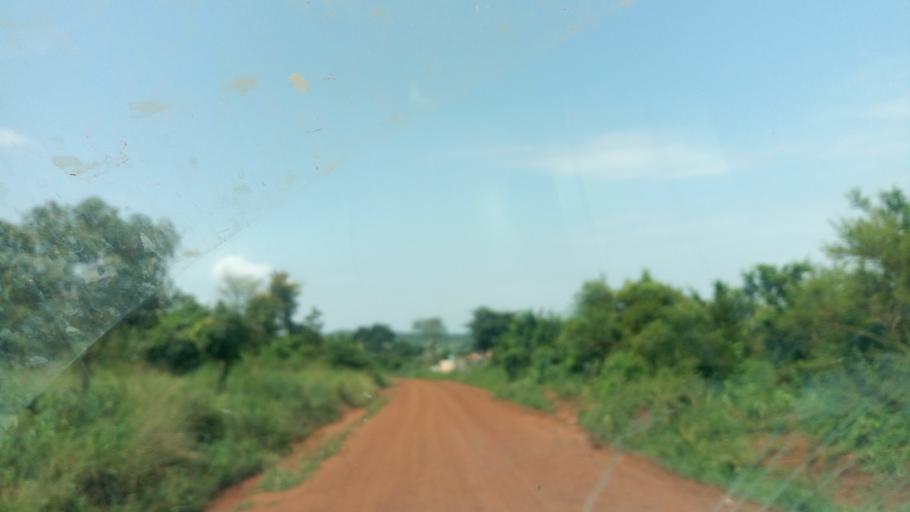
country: UG
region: Western Region
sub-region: Masindi District
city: Masindi
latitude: 1.6763
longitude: 31.8295
